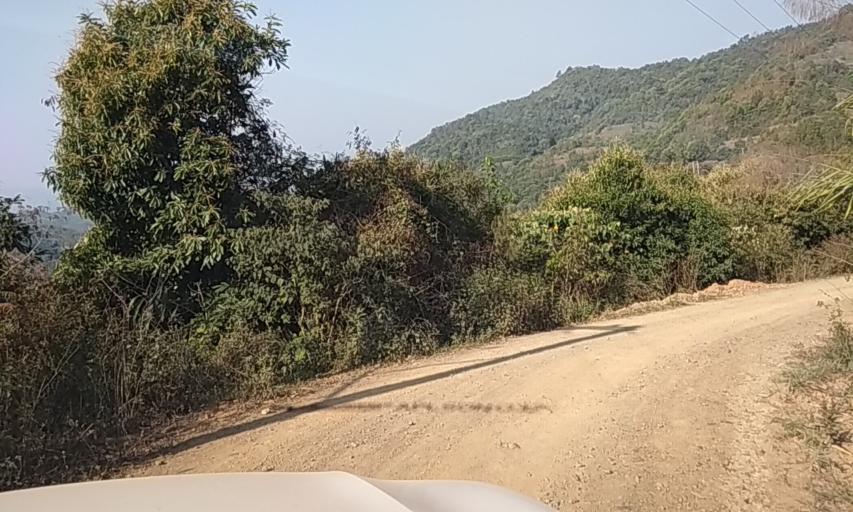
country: LA
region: Phongsali
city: Phongsali
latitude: 21.6929
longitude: 102.0899
